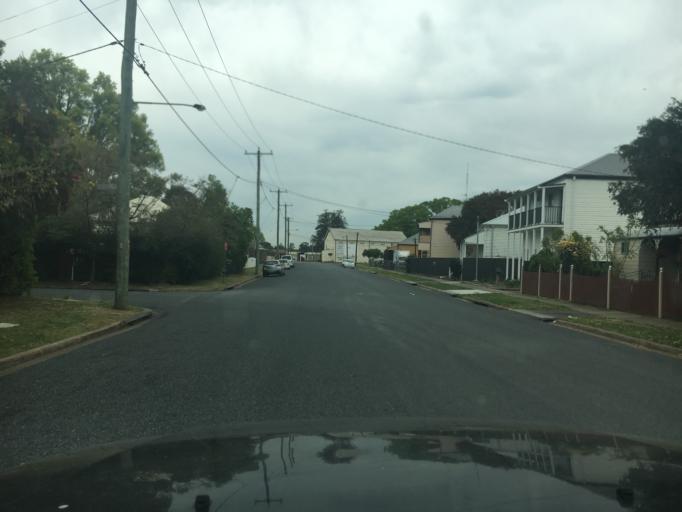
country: AU
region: New South Wales
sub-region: Maitland Municipality
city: Lorn
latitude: -32.7425
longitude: 151.5642
